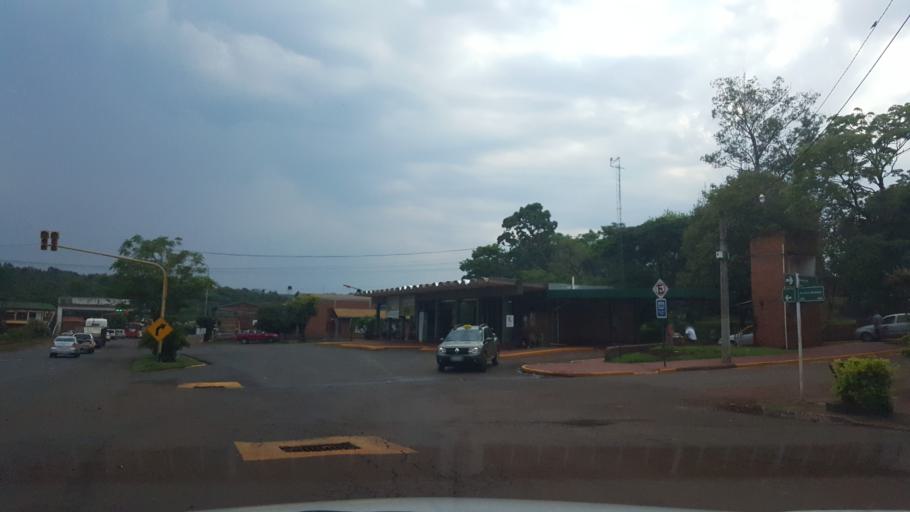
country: AR
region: Misiones
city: Capiovi
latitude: -26.9273
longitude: -55.0600
